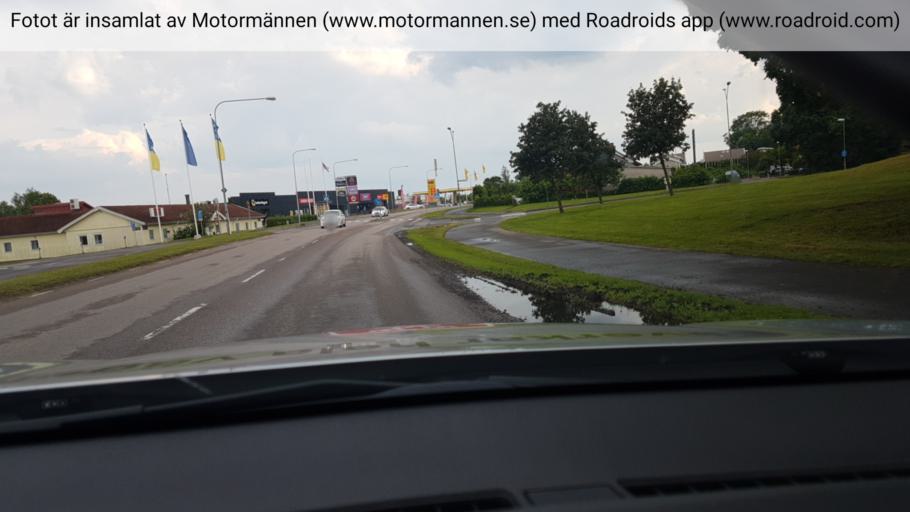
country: SE
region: Vaestra Goetaland
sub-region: Skovde Kommun
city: Skoevde
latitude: 58.4054
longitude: 13.8659
